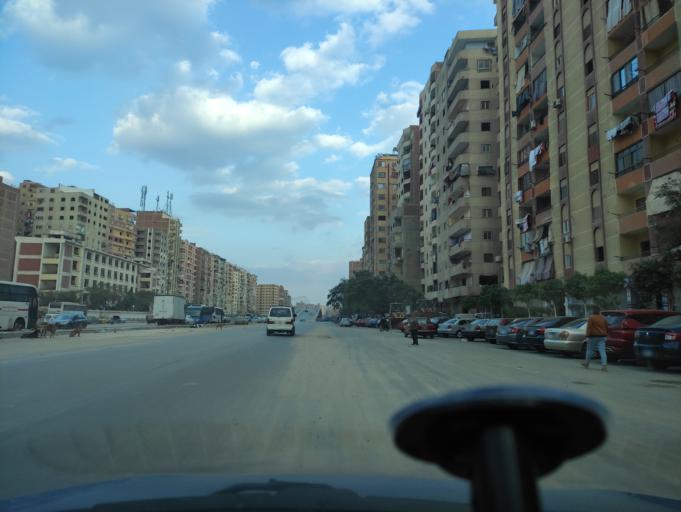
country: EG
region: Muhafazat al Qalyubiyah
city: Al Khankah
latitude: 30.1361
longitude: 31.3345
